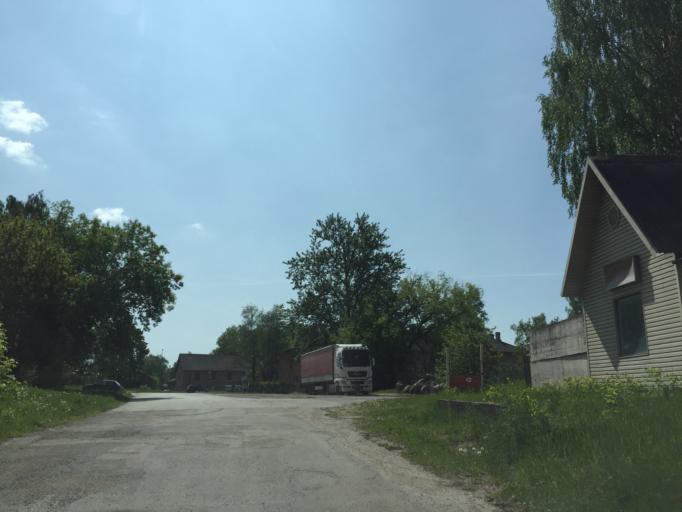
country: LV
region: Riga
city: Bergi
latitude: 56.9990
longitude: 24.2679
